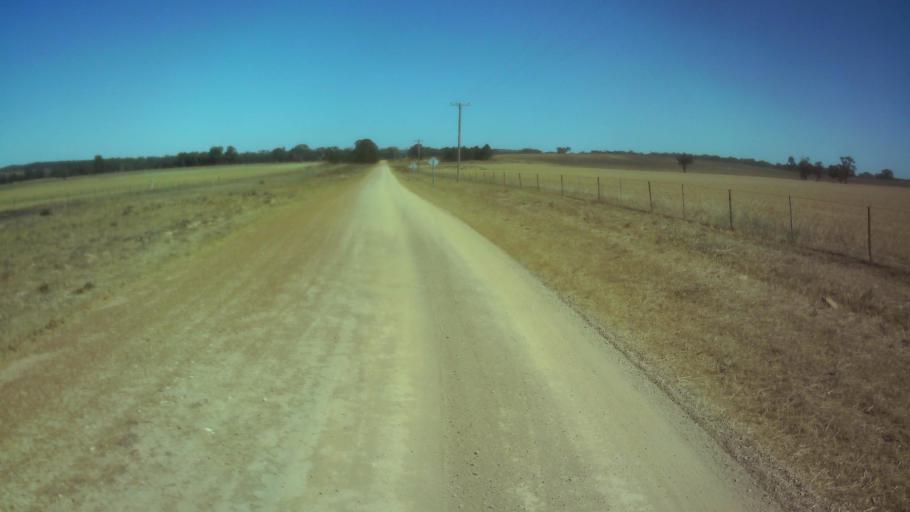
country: AU
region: New South Wales
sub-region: Weddin
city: Grenfell
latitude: -33.9375
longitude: 148.2856
